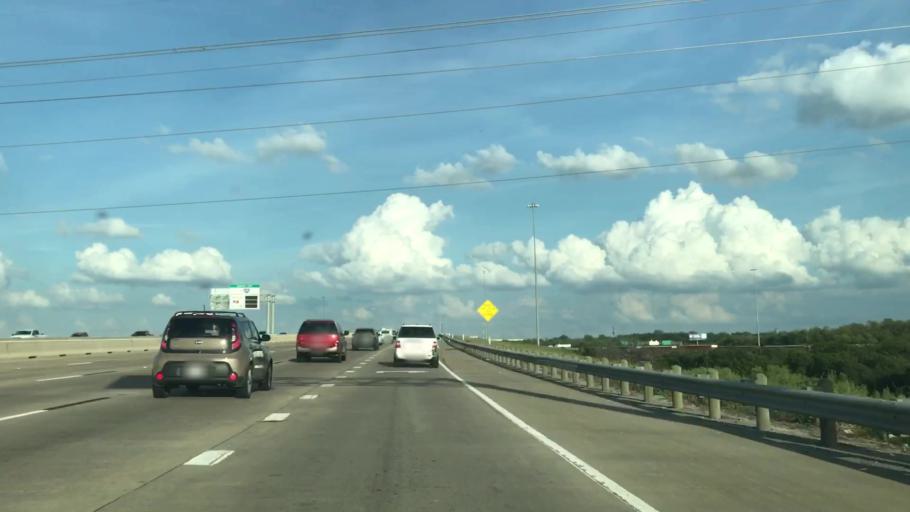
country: US
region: Texas
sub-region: Dallas County
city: Cockrell Hill
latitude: 32.7659
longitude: -96.9199
